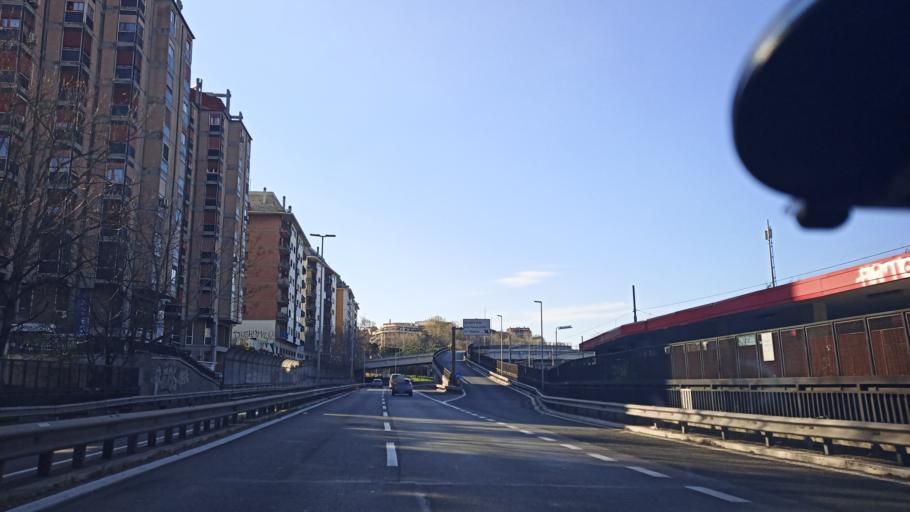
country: IT
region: Latium
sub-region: Citta metropolitana di Roma Capitale
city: Rome
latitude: 41.9324
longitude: 12.5234
